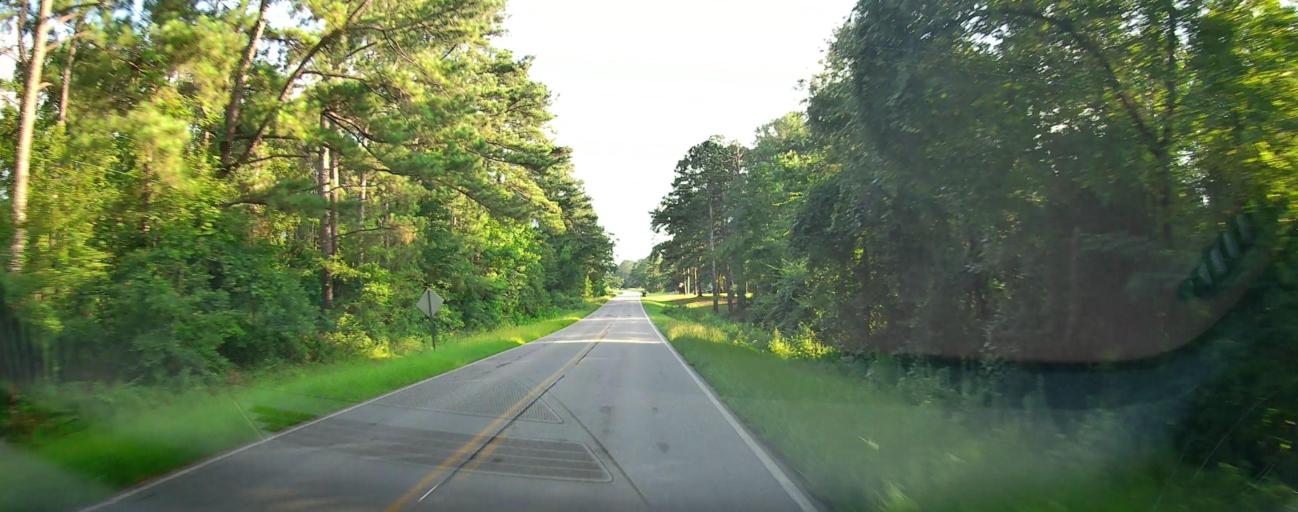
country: US
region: Georgia
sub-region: Peach County
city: Byron
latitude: 32.6893
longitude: -83.8545
